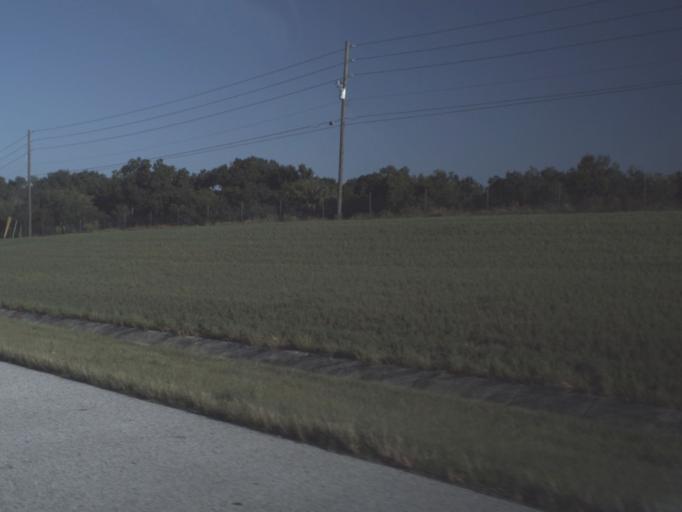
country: US
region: Florida
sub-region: Lake County
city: Montverde
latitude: 28.5643
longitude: -81.6865
